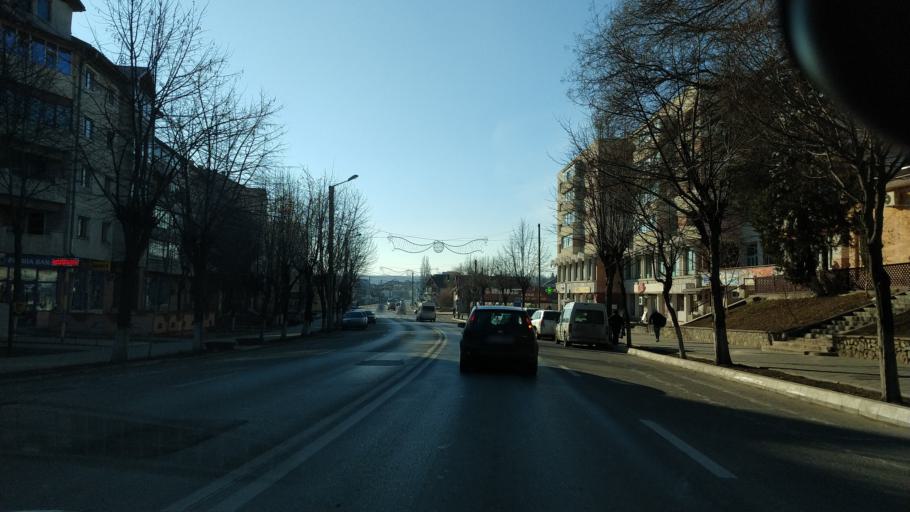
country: RO
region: Iasi
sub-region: Comuna Ion Neculce
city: Buznea
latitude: 47.2078
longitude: 27.0125
